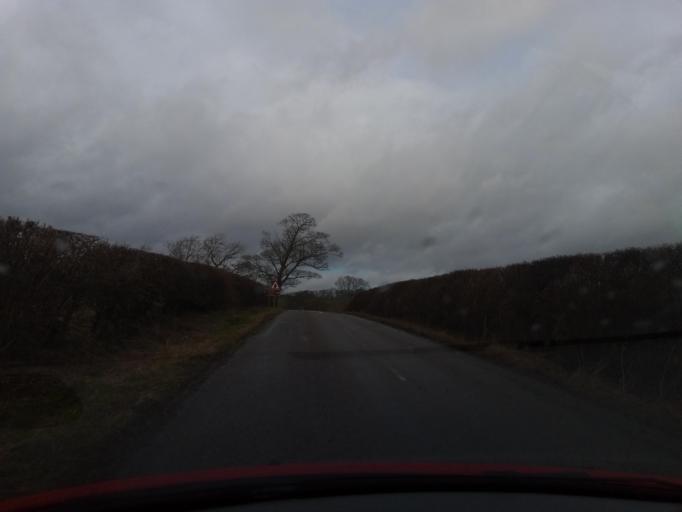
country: GB
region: England
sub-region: Northumberland
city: Rothley
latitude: 55.1858
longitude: -1.9695
